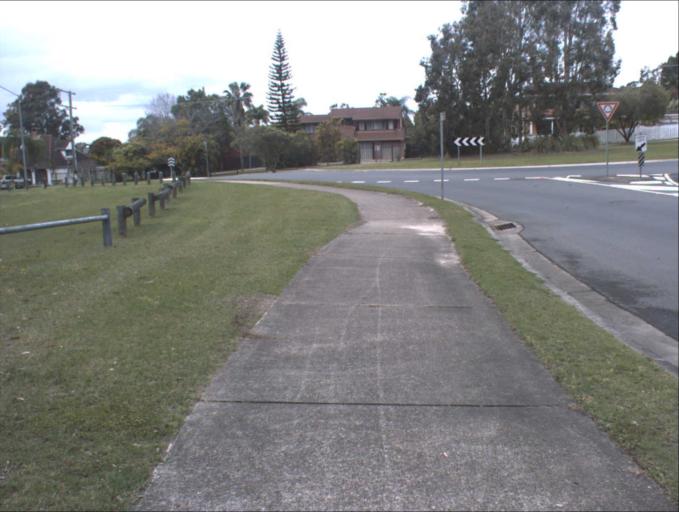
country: AU
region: Queensland
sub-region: Logan
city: Logan Reserve
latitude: -27.6787
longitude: 153.0613
